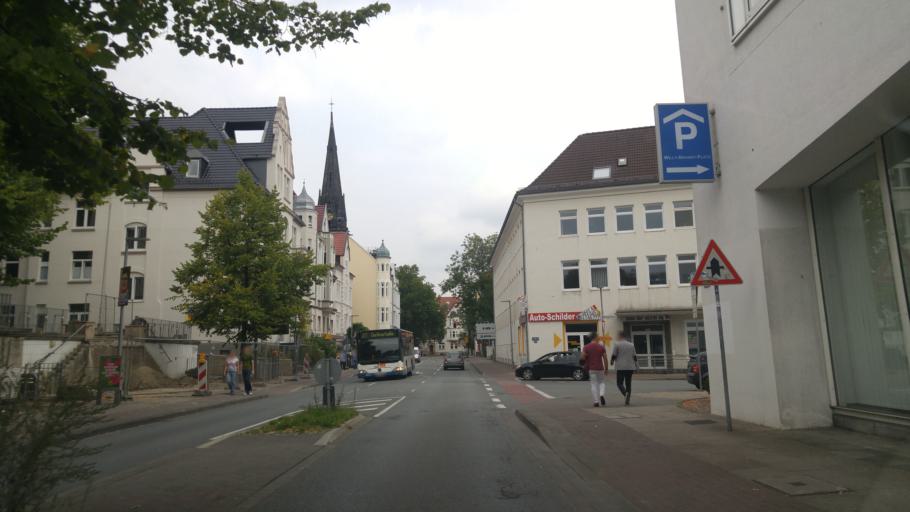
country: DE
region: North Rhine-Westphalia
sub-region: Regierungsbezirk Detmold
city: Bielefeld
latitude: 52.0268
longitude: 8.5377
